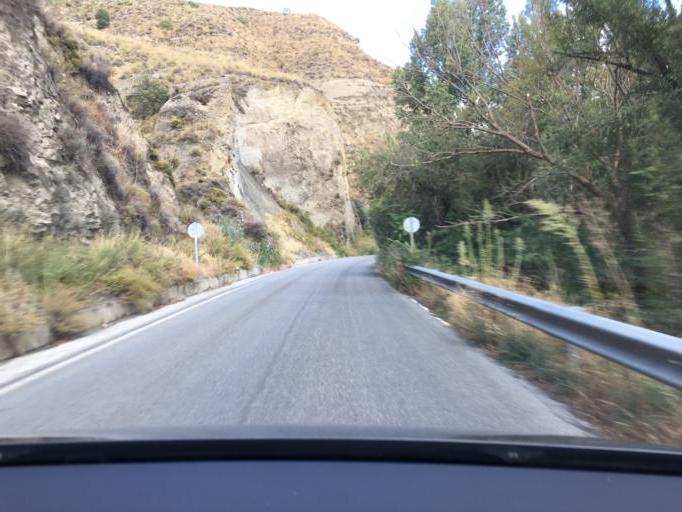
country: ES
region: Andalusia
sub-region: Provincia de Granada
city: Dudar
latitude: 37.1880
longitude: -3.4793
